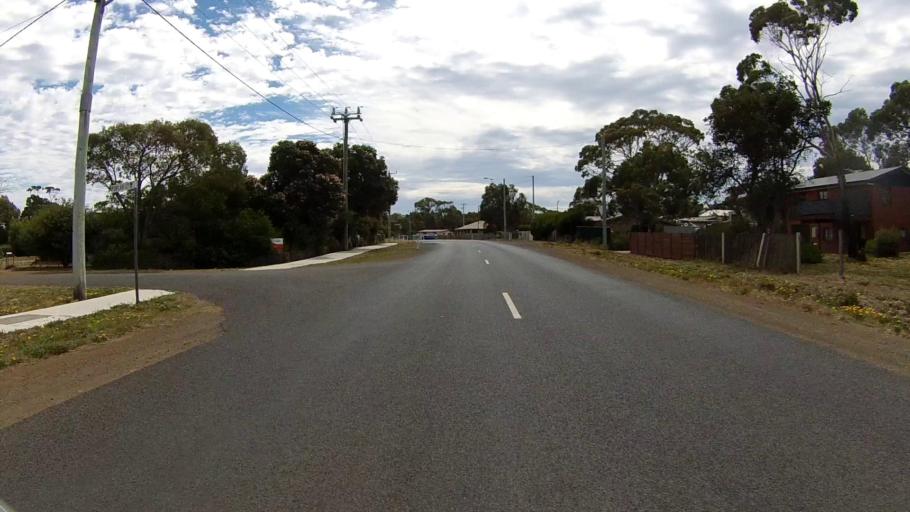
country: AU
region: Tasmania
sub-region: Sorell
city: Sorell
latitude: -42.8902
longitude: 147.6697
